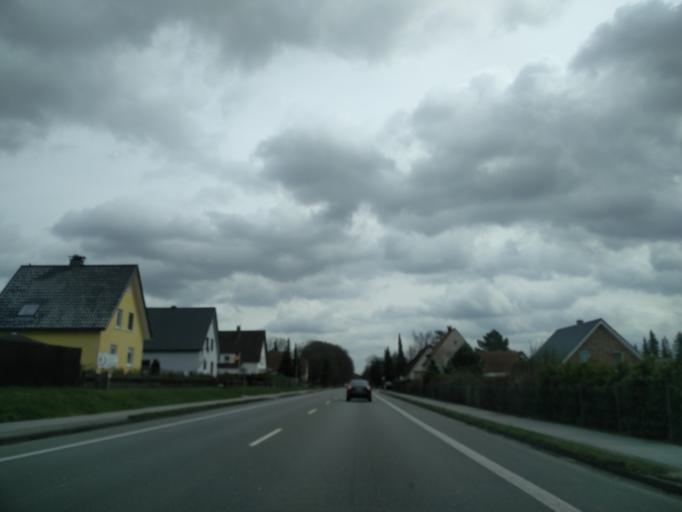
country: DE
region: North Rhine-Westphalia
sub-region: Regierungsbezirk Detmold
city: Steinhagen
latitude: 52.0200
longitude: 8.4319
